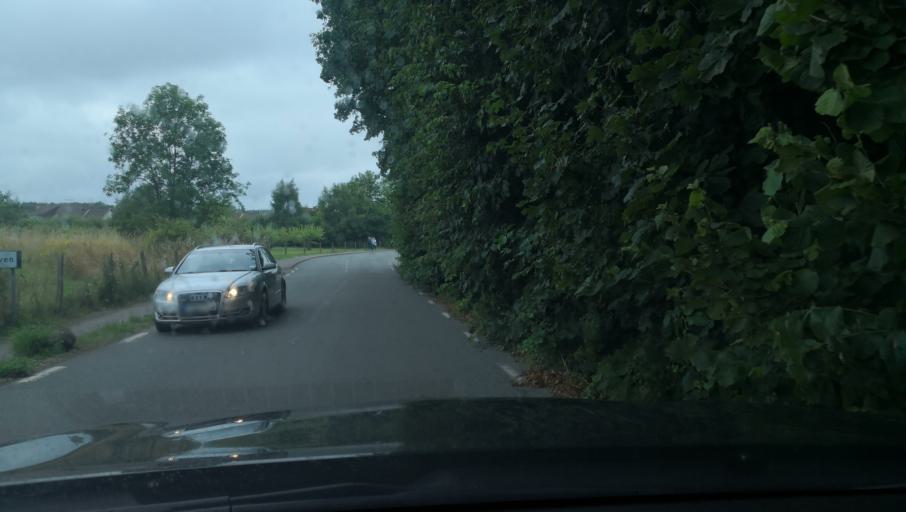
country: SE
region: Skane
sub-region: Simrishamns Kommun
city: Kivik
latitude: 55.6830
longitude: 14.2343
